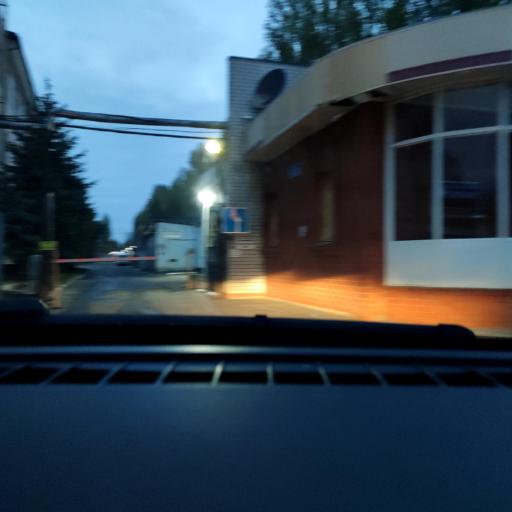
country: RU
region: Voronezj
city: Voronezh
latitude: 51.6300
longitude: 39.2374
